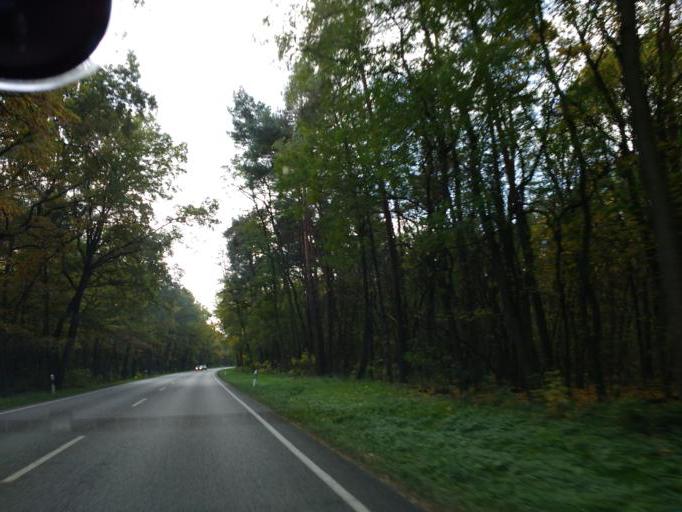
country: DE
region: Brandenburg
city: Petershagen
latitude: 52.5061
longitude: 13.7991
